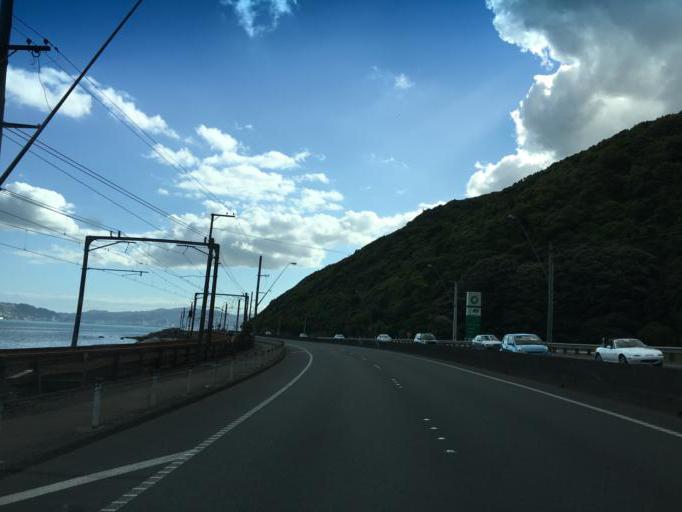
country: NZ
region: Wellington
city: Petone
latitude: -41.2322
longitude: 174.8380
